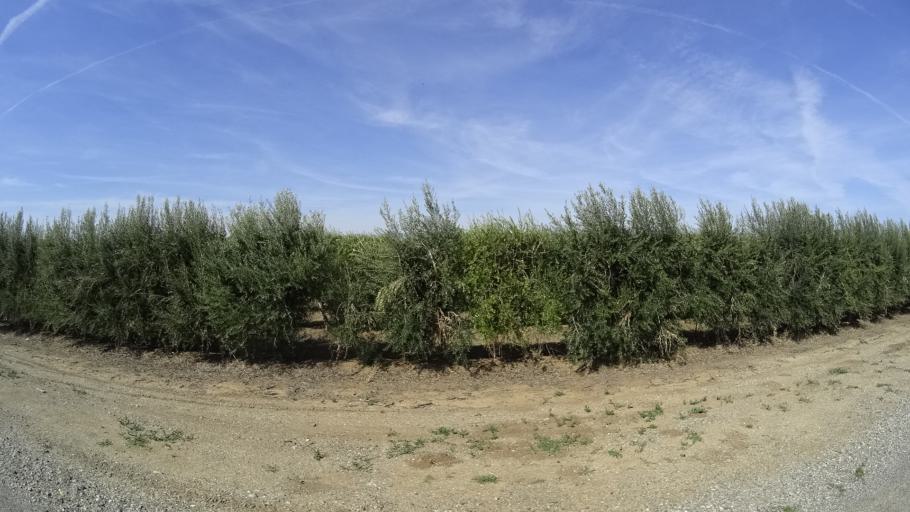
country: US
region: California
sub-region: Glenn County
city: Willows
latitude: 39.5266
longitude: -122.2869
